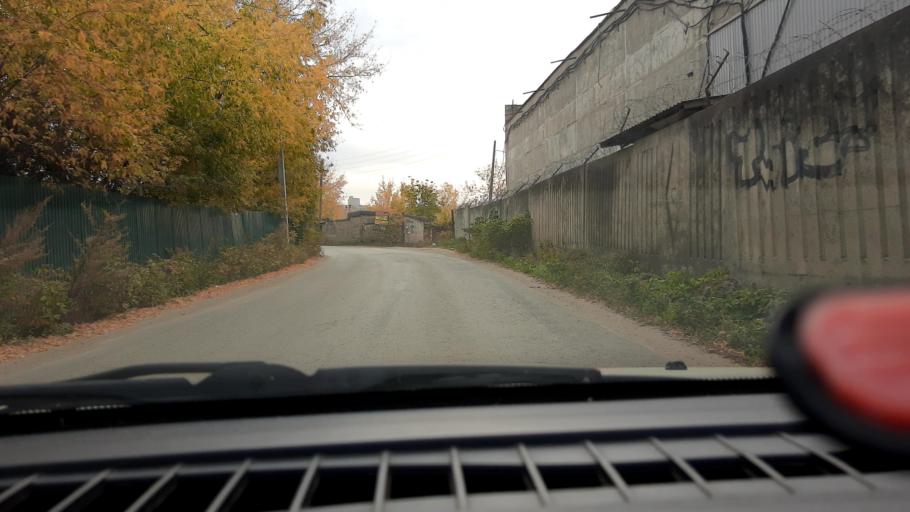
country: RU
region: Nizjnij Novgorod
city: Nizhniy Novgorod
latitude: 56.2667
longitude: 43.9480
